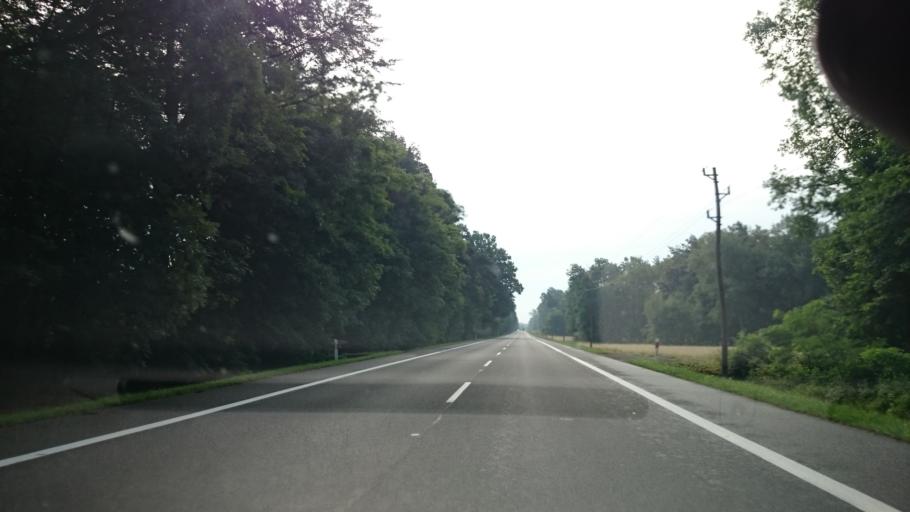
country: PL
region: Silesian Voivodeship
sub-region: Powiat gliwicki
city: Toszek
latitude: 50.4810
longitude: 18.4394
